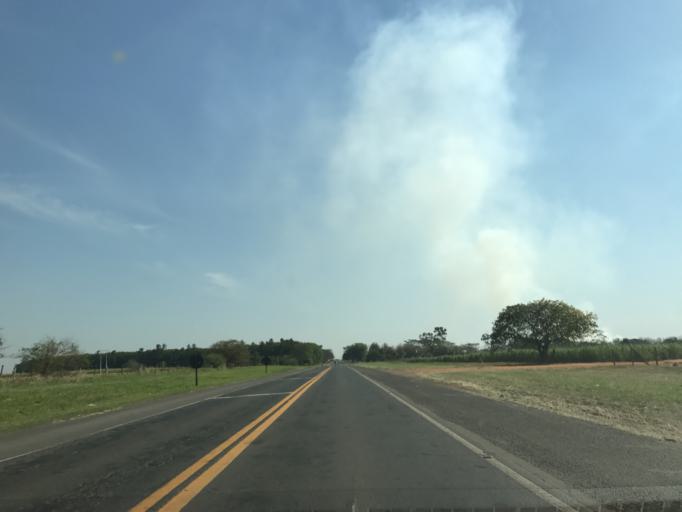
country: BR
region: Sao Paulo
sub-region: Penapolis
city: Penapolis
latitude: -21.3882
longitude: -50.0980
